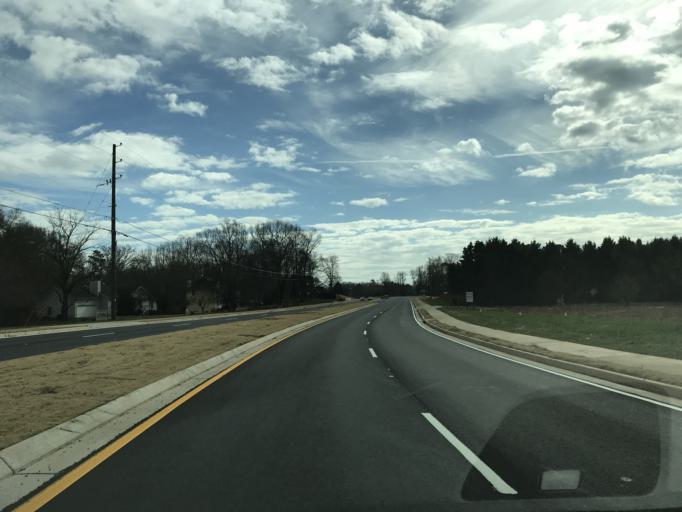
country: US
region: Georgia
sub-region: Forsyth County
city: Cumming
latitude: 34.1227
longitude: -84.1674
